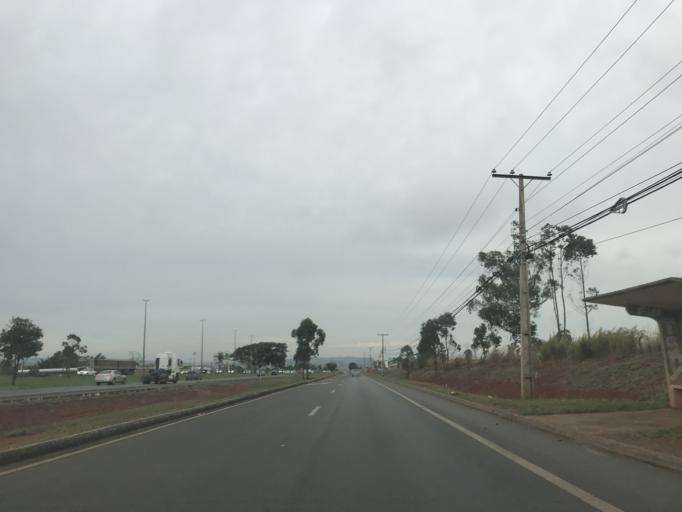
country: BR
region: Federal District
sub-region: Brasilia
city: Brasilia
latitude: -15.6835
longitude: -47.8419
